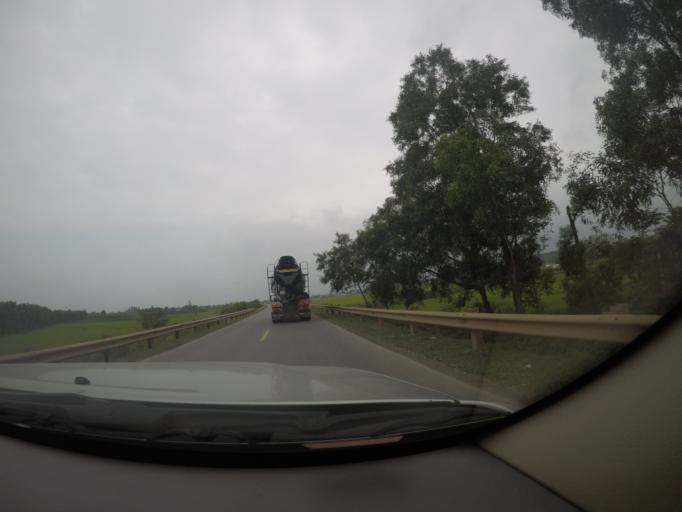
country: VN
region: Quang Binh
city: Kien Giang
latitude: 17.2428
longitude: 106.6866
